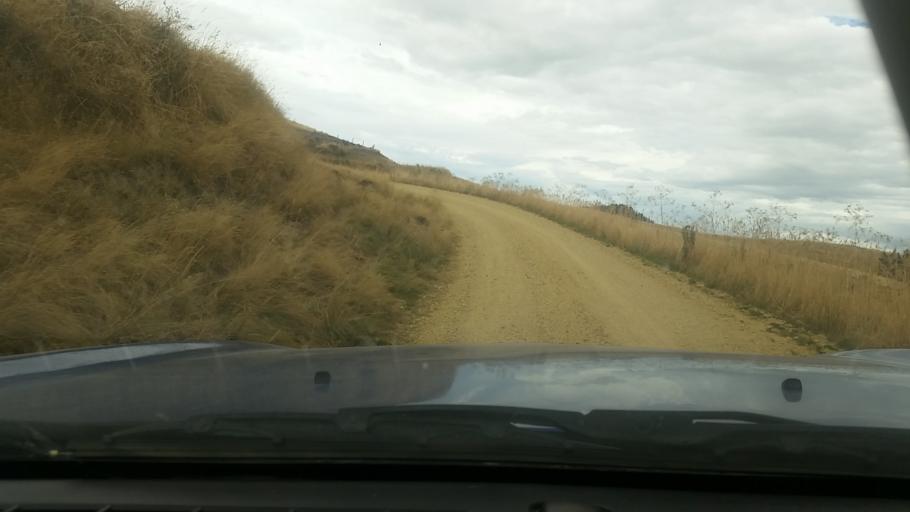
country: NZ
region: Southland
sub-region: Gore District
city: Gore
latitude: -45.5830
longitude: 169.3934
